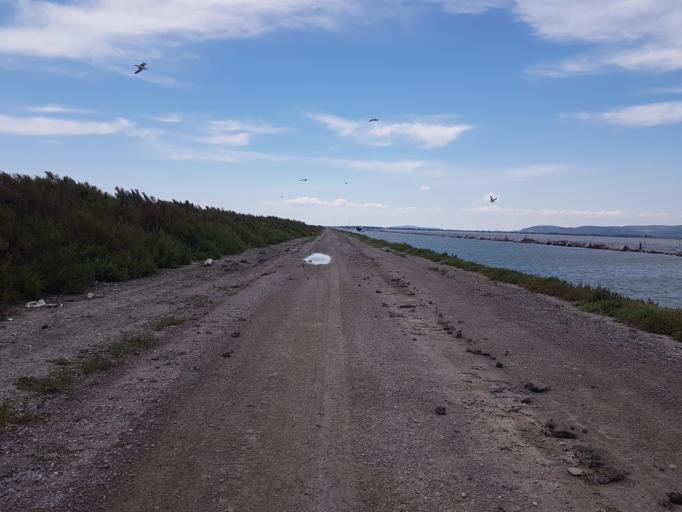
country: FR
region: Languedoc-Roussillon
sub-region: Departement de l'Herault
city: Villeneuve-les-Maguelone
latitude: 43.4980
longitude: 3.8559
